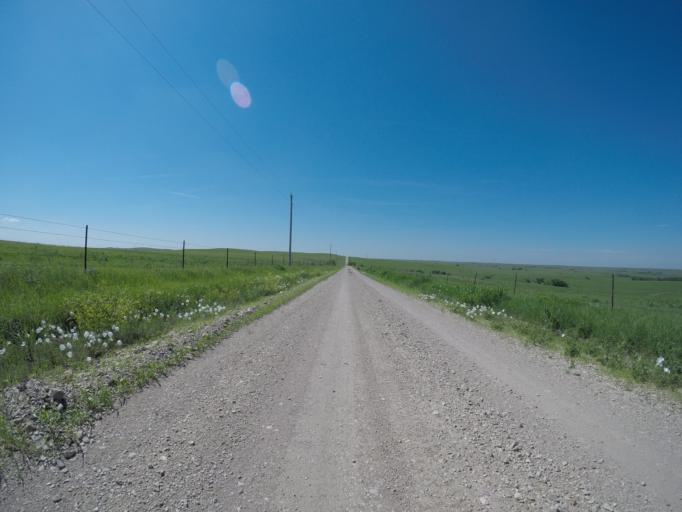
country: US
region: Kansas
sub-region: Wabaunsee County
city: Alma
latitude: 39.0090
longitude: -96.1783
